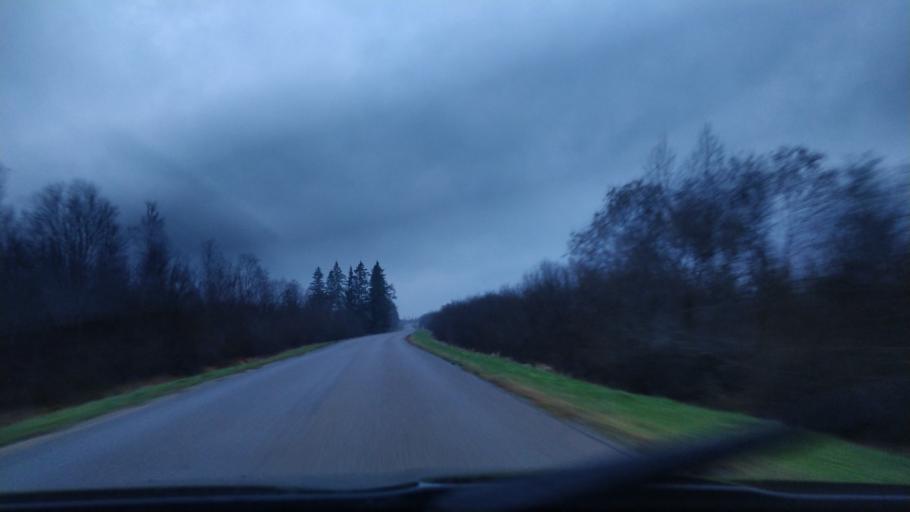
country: EE
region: Laeaene
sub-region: Lihula vald
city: Lihula
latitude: 58.7019
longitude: 23.8589
